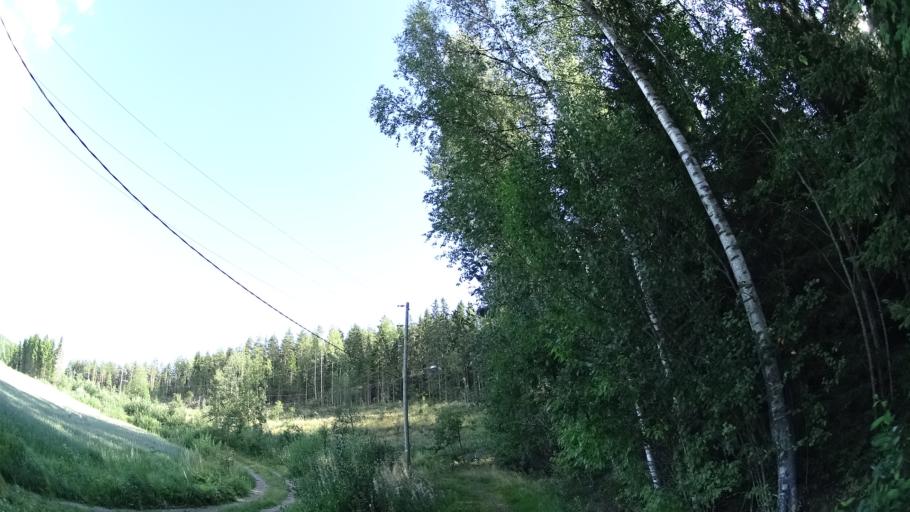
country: FI
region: Uusimaa
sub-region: Helsinki
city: Vihti
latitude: 60.3782
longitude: 24.3785
